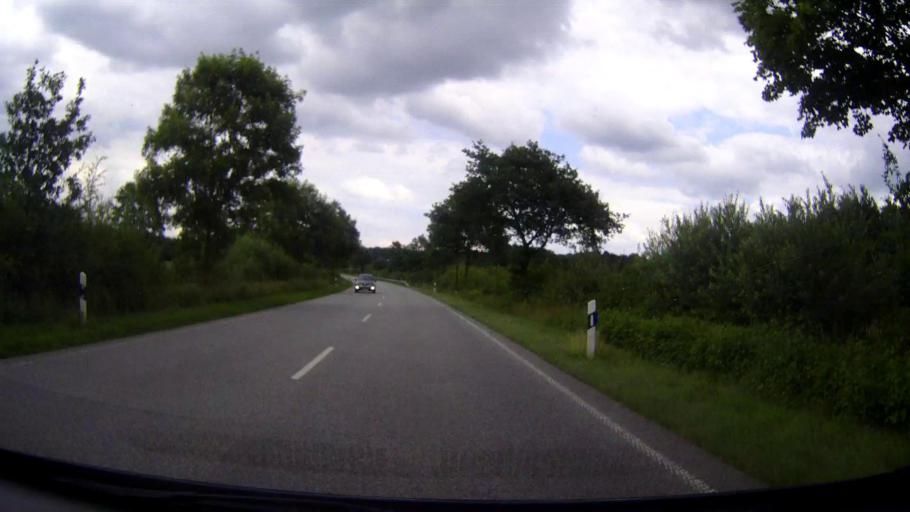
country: DE
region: Schleswig-Holstein
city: Jahrsdorf
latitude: 54.0747
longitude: 9.6275
